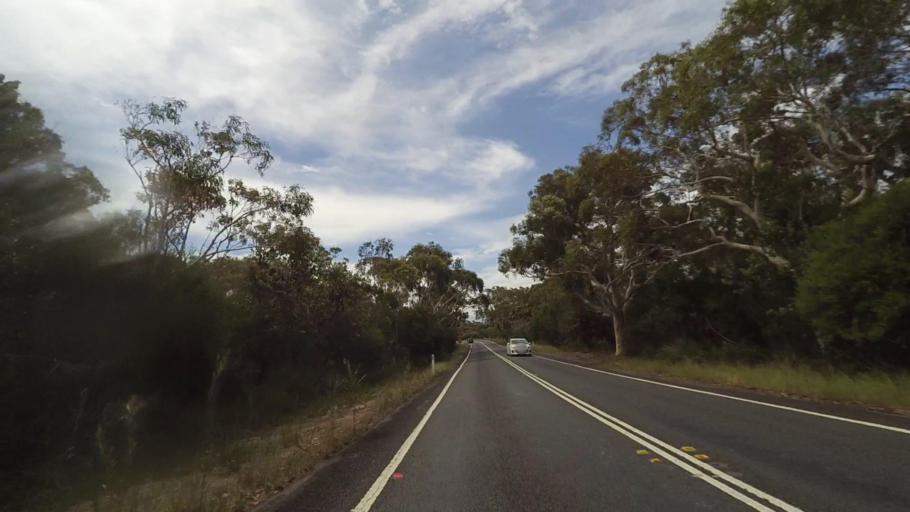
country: AU
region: New South Wales
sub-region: Sutherland Shire
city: Grays Point
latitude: -34.0840
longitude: 151.0637
